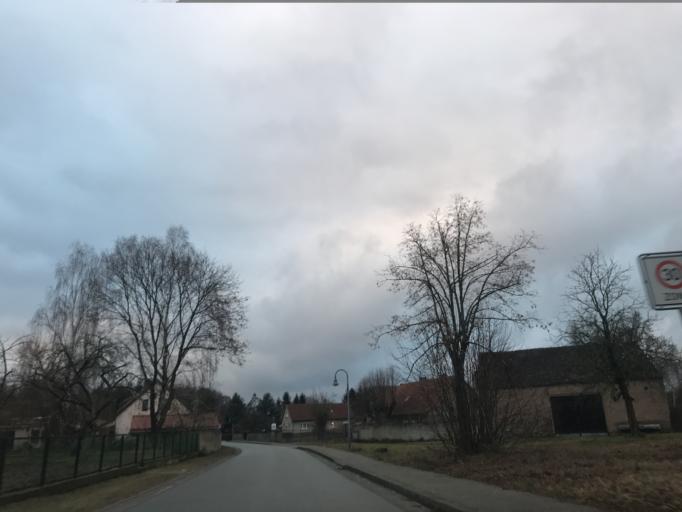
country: DE
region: Brandenburg
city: Rheinsberg
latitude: 53.1352
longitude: 12.7858
